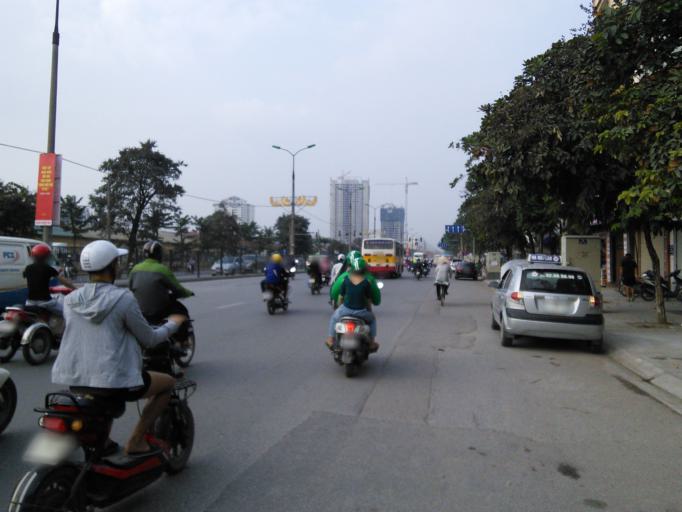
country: VN
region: Ha Noi
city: Van Dien
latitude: 20.9784
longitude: 105.8411
